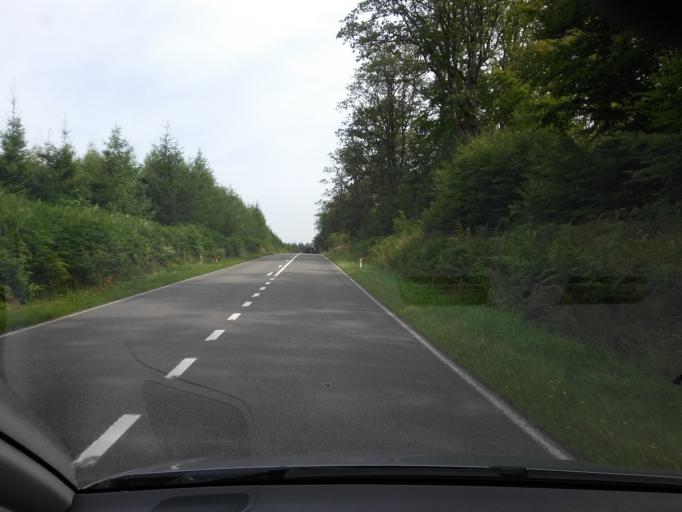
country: BE
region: Wallonia
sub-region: Province du Luxembourg
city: Chiny
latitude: 49.7667
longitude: 5.3220
